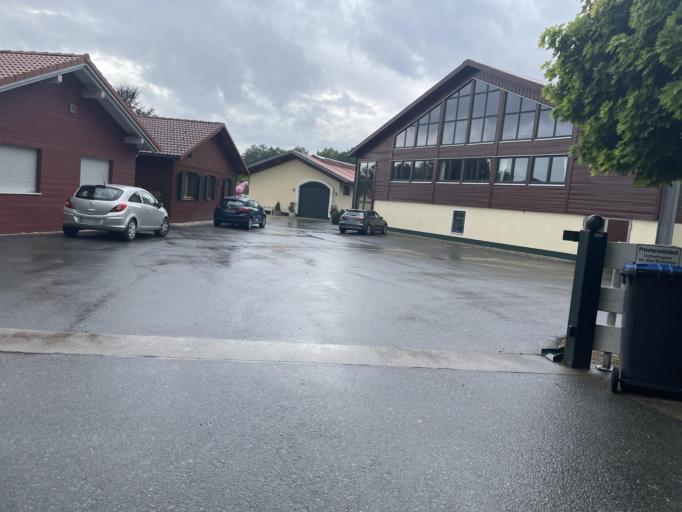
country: DE
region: Bavaria
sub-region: Upper Franconia
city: Neunkirchen am Main
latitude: 49.9385
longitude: 11.6400
